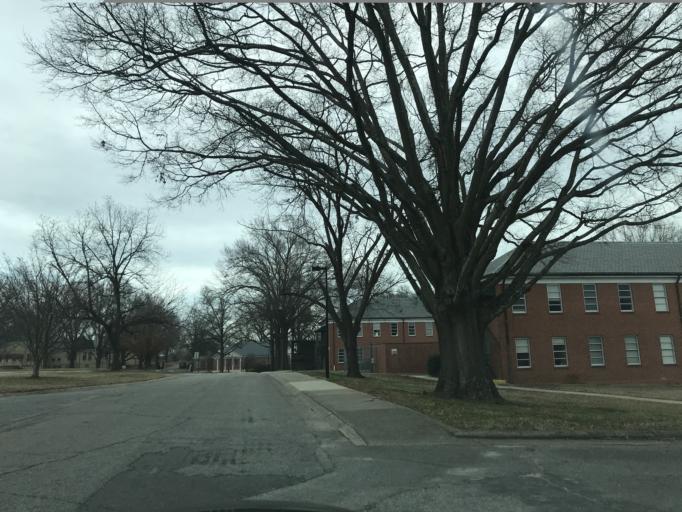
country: US
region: North Carolina
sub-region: Wake County
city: Raleigh
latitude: 35.7680
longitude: -78.6570
